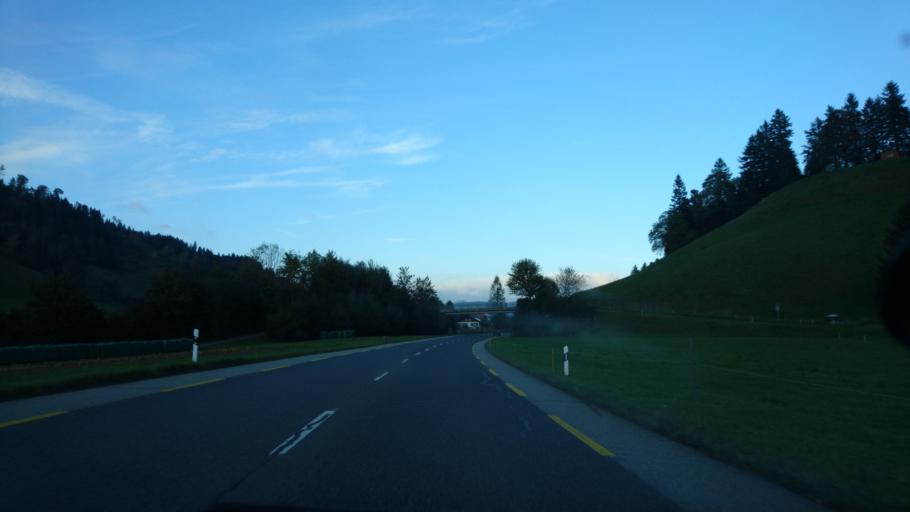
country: CH
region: Bern
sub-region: Emmental District
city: Signau
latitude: 46.9120
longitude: 7.7180
